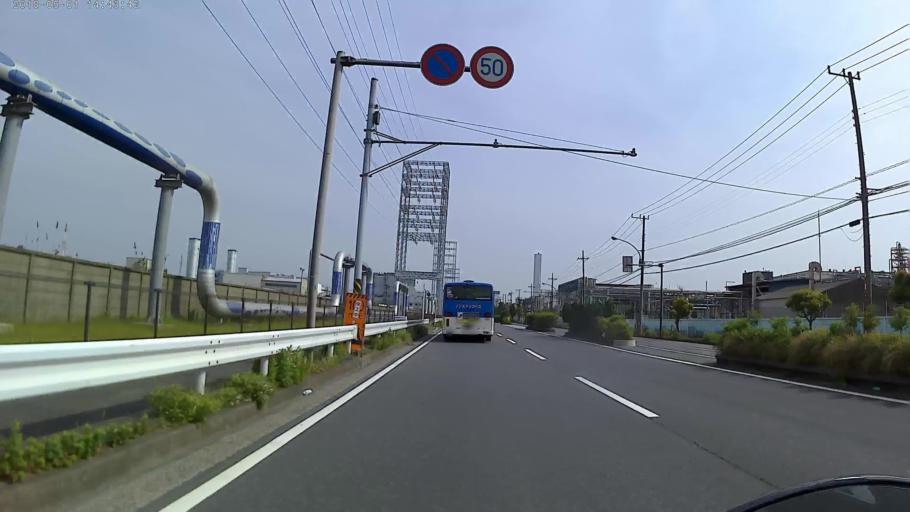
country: JP
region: Kanagawa
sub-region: Kawasaki-shi
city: Kawasaki
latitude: 35.5192
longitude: 139.7567
